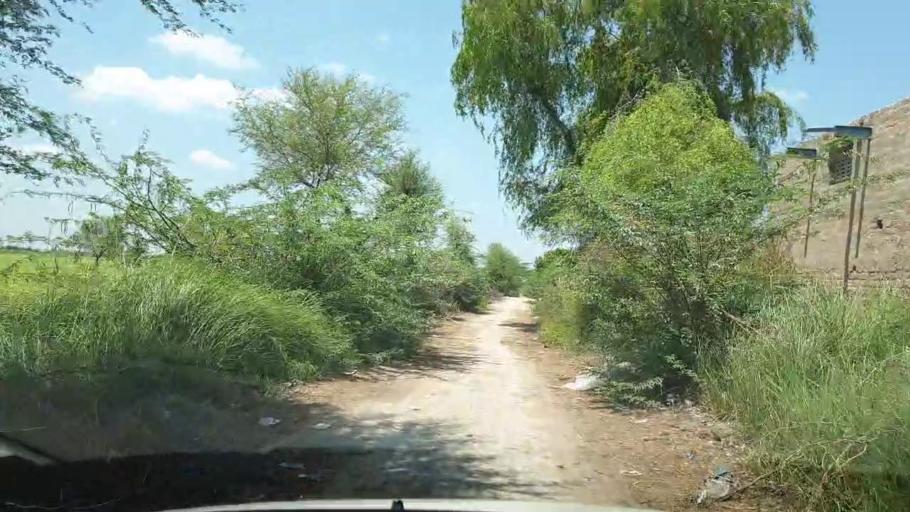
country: PK
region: Sindh
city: Sanghar
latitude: 26.0714
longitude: 69.0478
